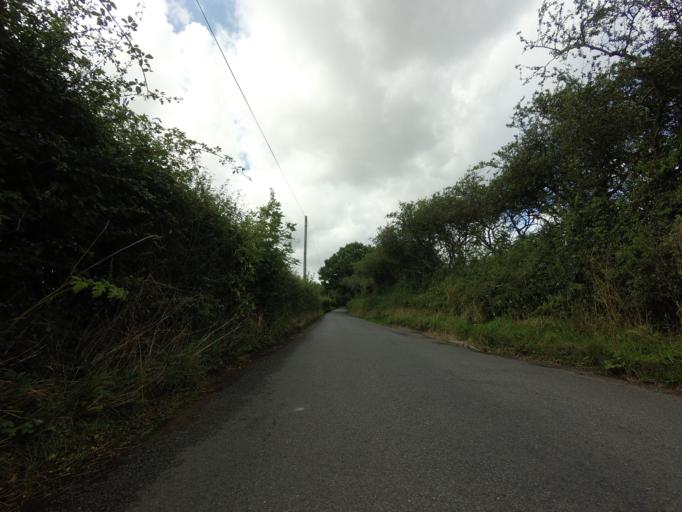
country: GB
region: England
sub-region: Kent
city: Hadlow
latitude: 51.2388
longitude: 0.3254
